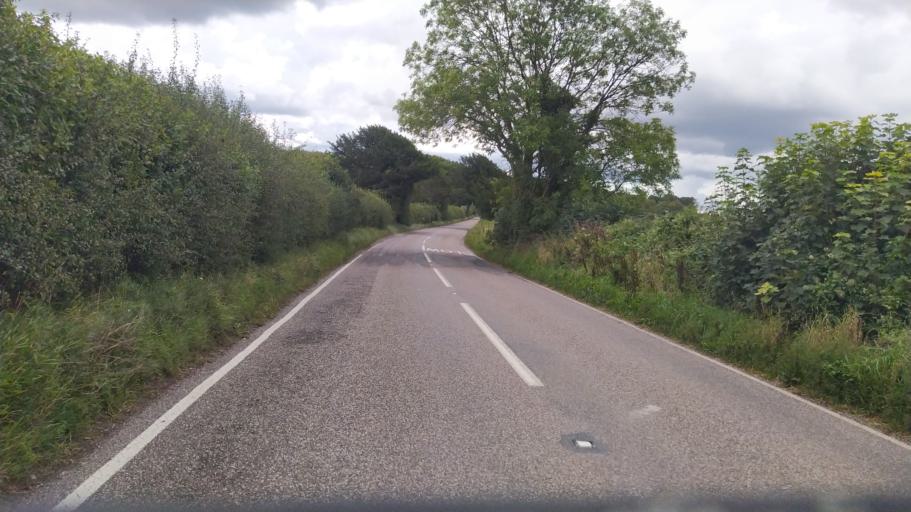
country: GB
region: England
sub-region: Wiltshire
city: Bower Chalke
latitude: 50.9210
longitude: -1.9450
